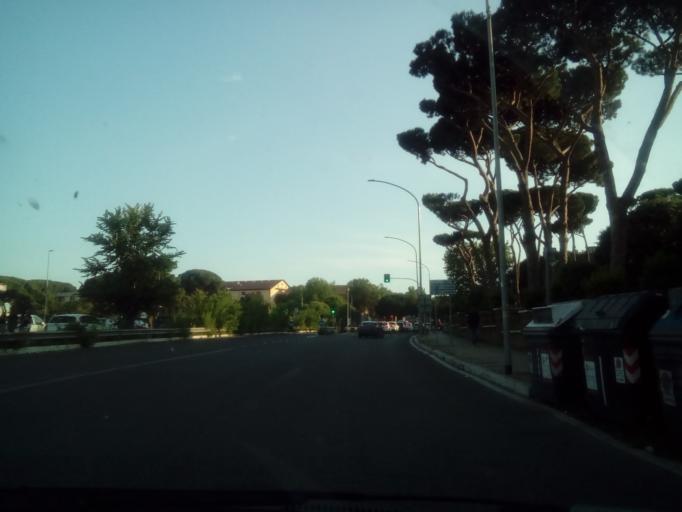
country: IT
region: Latium
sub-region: Citta metropolitana di Roma Capitale
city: Ciampino
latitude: 41.8538
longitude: 12.5706
